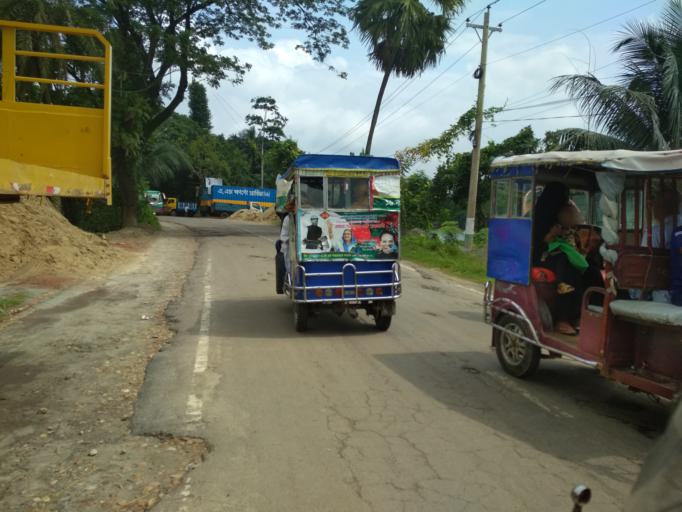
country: BD
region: Chittagong
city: Lakshmipur
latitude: 22.9671
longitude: 90.8098
